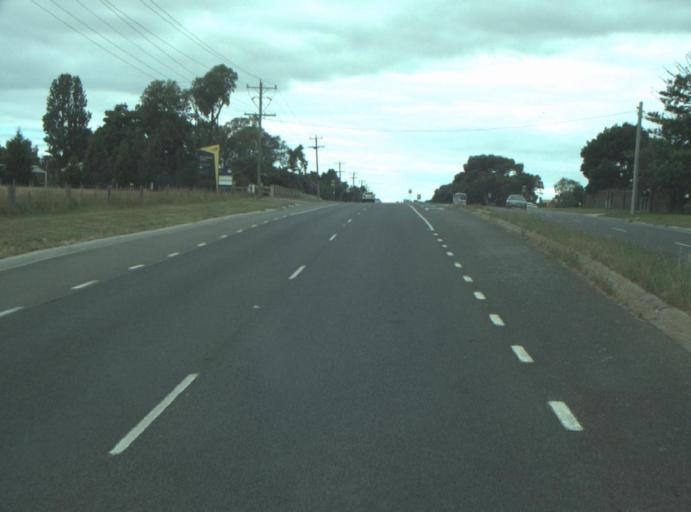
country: AU
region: Victoria
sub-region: Greater Geelong
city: Breakwater
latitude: -38.2147
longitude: 144.3388
